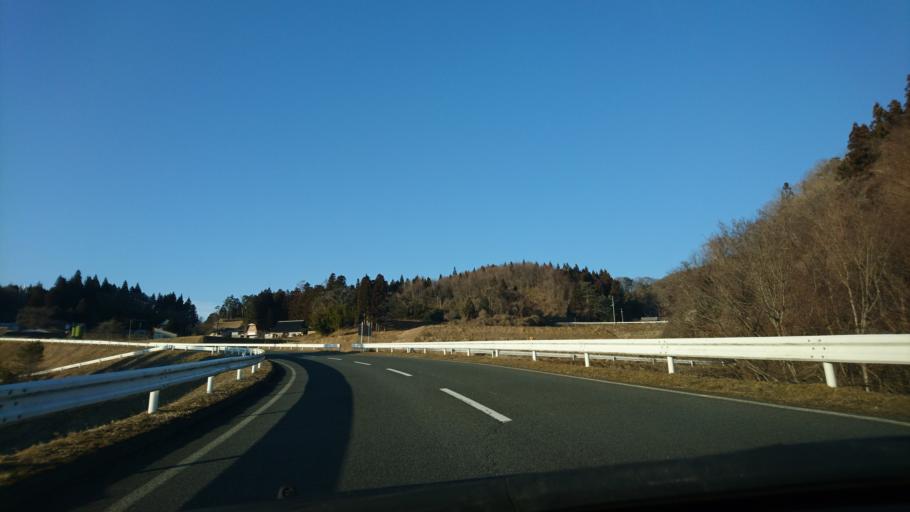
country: JP
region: Iwate
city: Mizusawa
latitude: 39.0253
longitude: 141.3754
